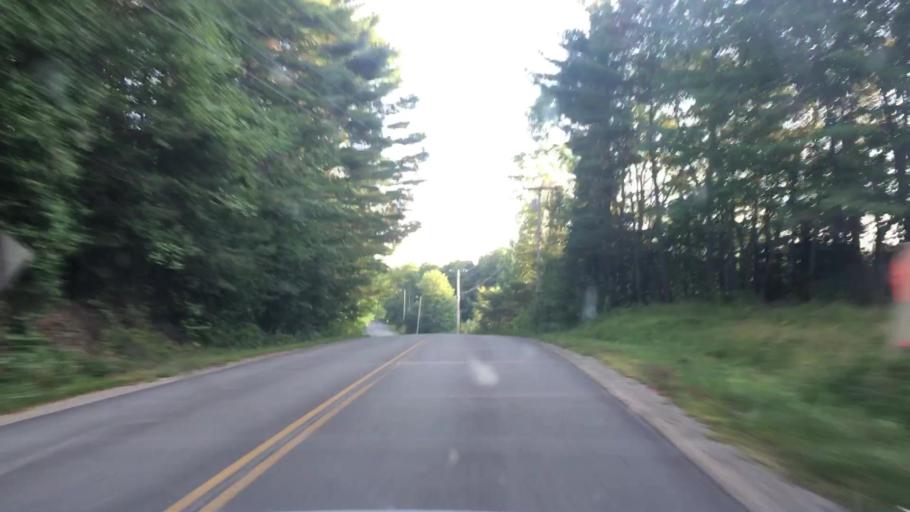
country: US
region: Maine
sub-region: Penobscot County
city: Hampden
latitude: 44.7104
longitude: -68.8874
